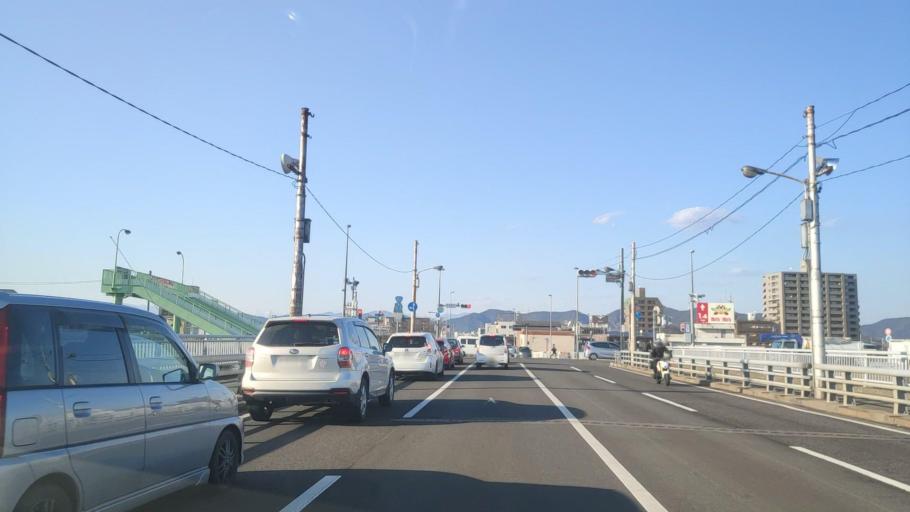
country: JP
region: Gifu
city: Gifu-shi
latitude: 35.4311
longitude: 136.7500
